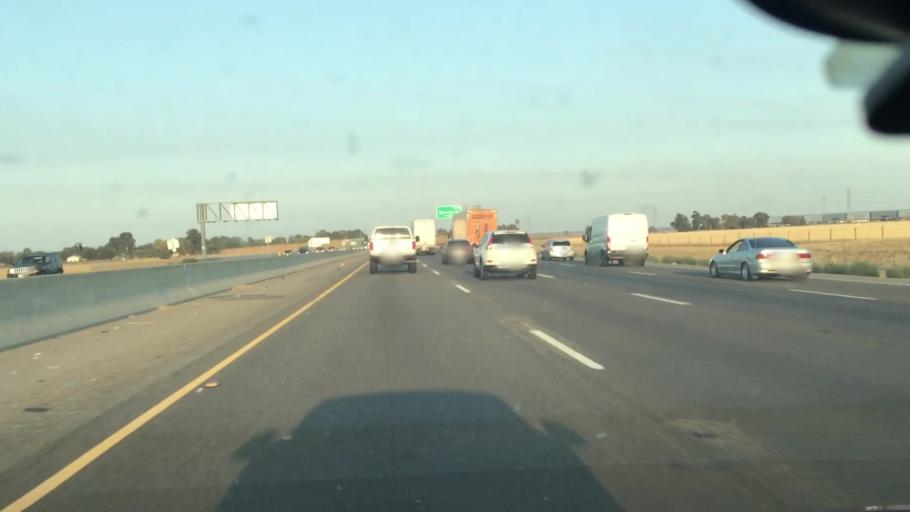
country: US
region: California
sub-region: San Joaquin County
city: Mountain House
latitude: 37.7414
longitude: -121.5227
